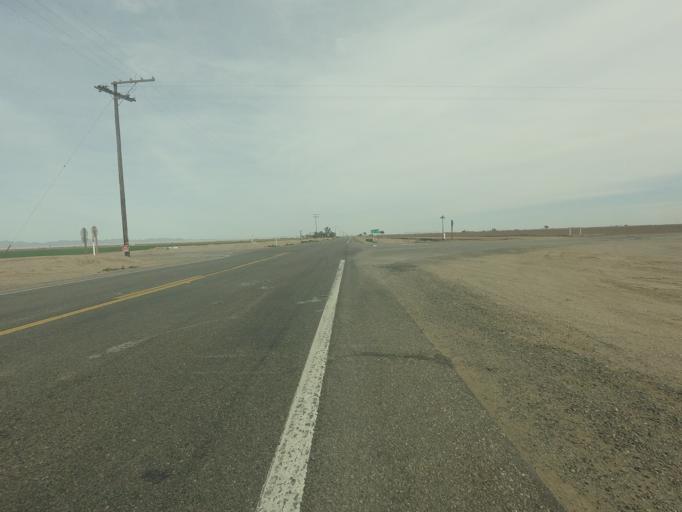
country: US
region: California
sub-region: Imperial County
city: Brawley
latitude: 32.9746
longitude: -115.3722
